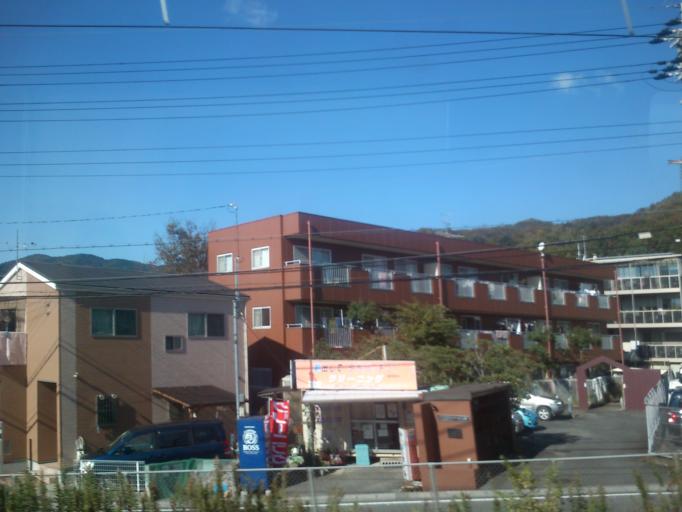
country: JP
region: Kyoto
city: Yawata
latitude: 34.8896
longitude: 135.6708
